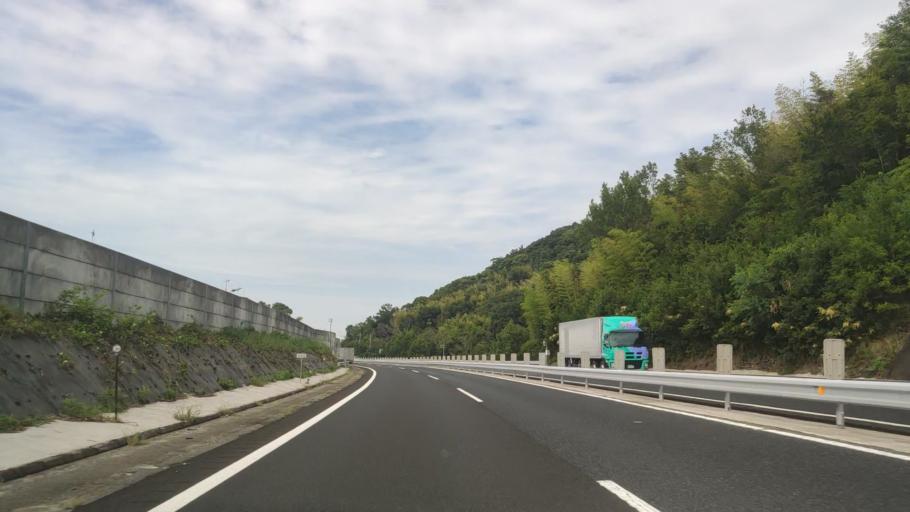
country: JP
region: Wakayama
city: Wakayama-shi
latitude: 34.2202
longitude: 135.2213
